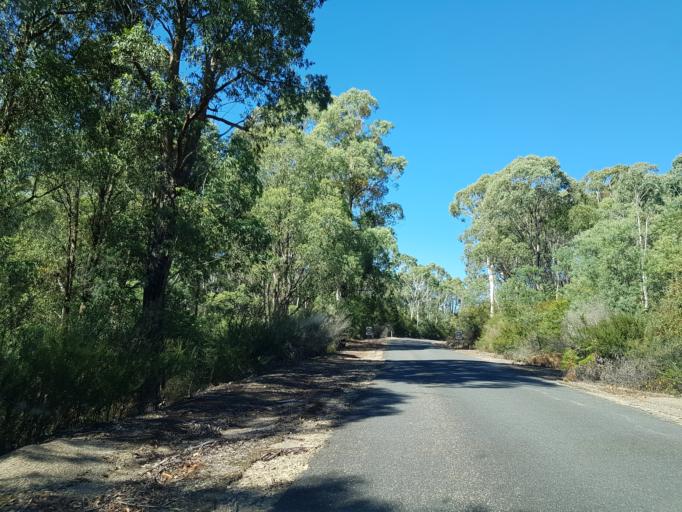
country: AU
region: Victoria
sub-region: Mansfield
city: Mansfield
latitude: -36.8989
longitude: 146.3885
